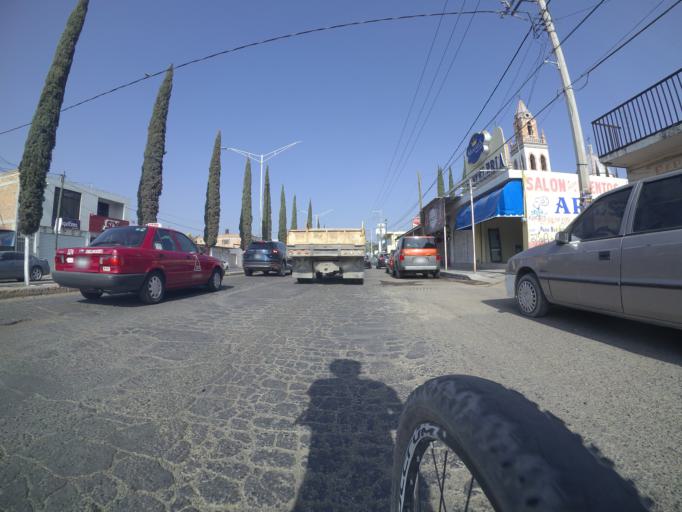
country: MX
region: Aguascalientes
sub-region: Jesus Maria
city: Corral de Barrancos
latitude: 21.9514
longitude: -102.3277
